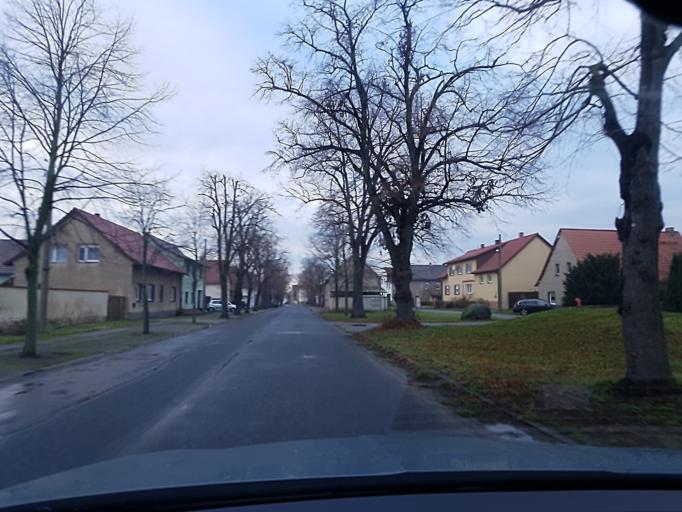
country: DE
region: Brandenburg
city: Schilda
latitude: 51.5776
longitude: 13.3647
